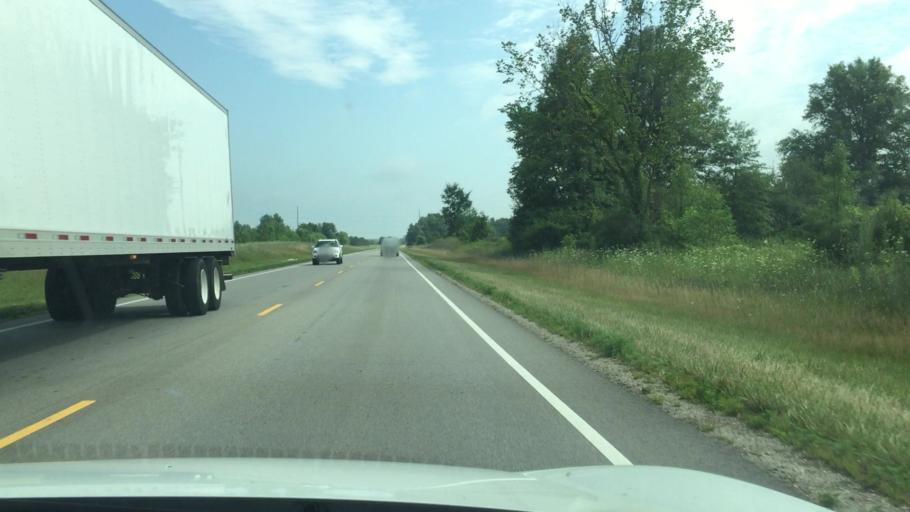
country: US
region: Ohio
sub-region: Union County
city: Marysville
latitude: 40.2178
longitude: -83.3974
